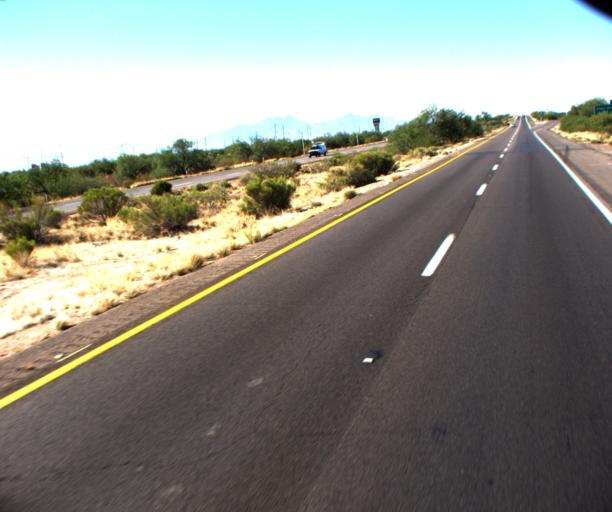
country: US
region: Arizona
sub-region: Pima County
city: Sahuarita
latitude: 32.0089
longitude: -110.9925
